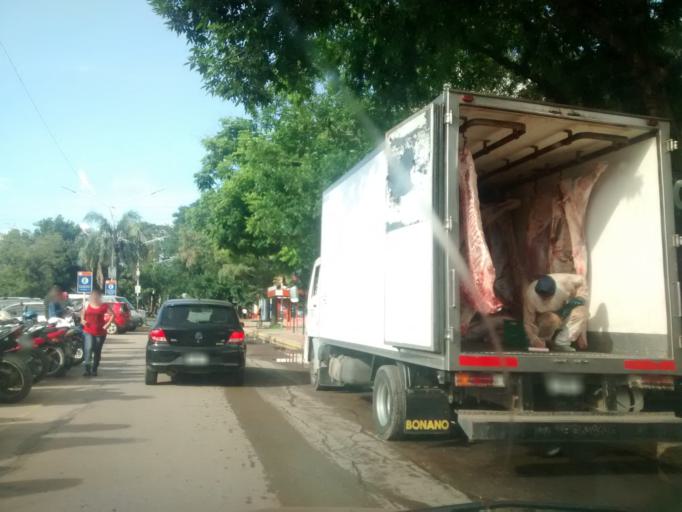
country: AR
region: Chaco
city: Resistencia
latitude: -27.4538
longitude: -58.9808
